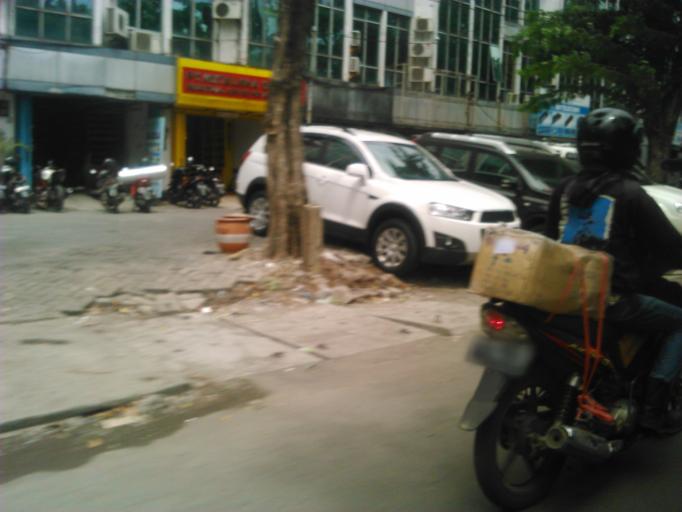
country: ID
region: East Java
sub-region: Kota Surabaya
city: Surabaya
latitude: -7.2499
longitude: 112.7309
